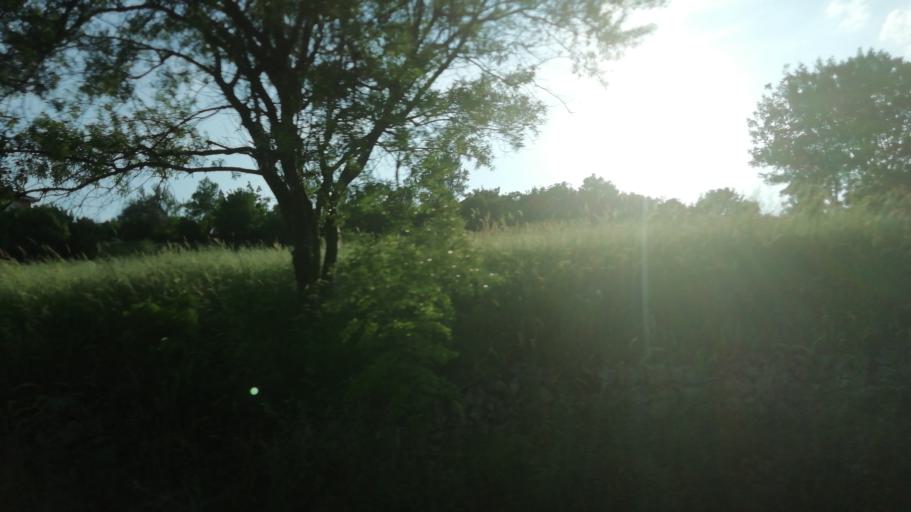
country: TR
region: Karabuk
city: Karabuk
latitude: 41.1287
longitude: 32.6217
